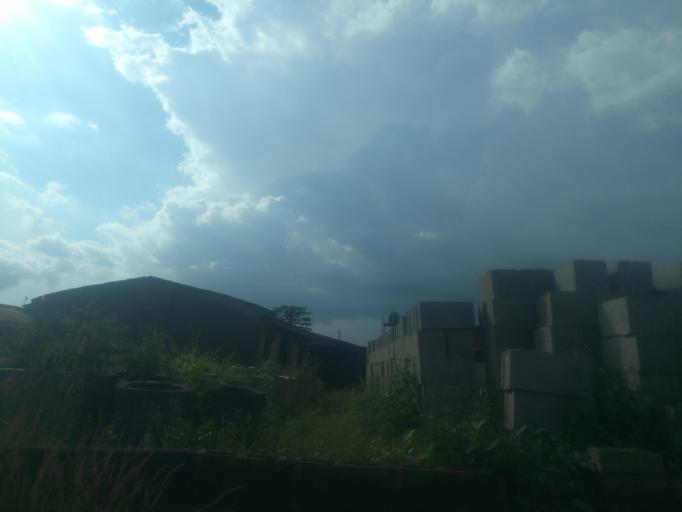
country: NG
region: Oyo
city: Ibadan
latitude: 7.4187
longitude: 3.8423
